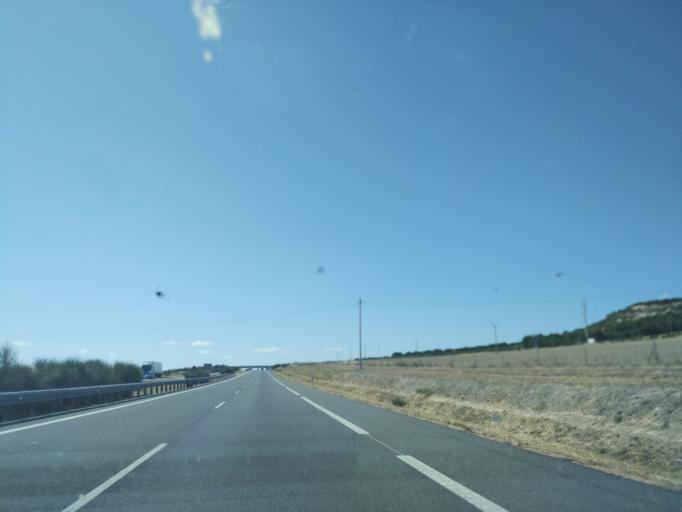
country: ES
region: Castille and Leon
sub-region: Provincia de Valladolid
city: Bercero
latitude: 41.5295
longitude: -5.0517
